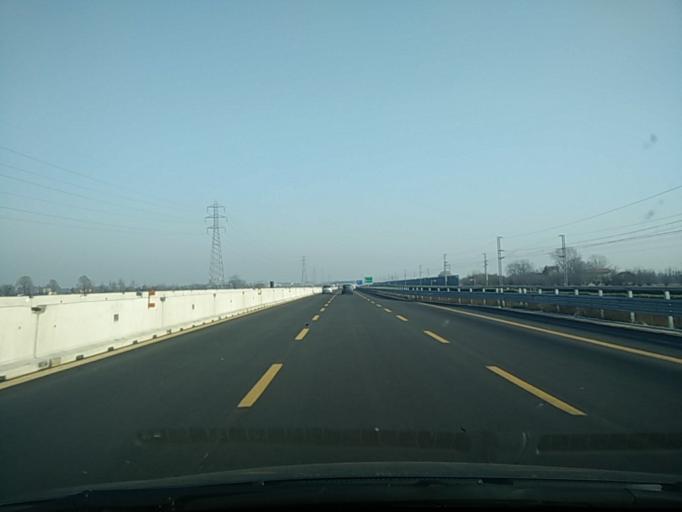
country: IT
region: Lombardy
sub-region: Citta metropolitana di Milano
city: Santo Stefano Ticino
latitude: 45.4977
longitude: 8.9105
